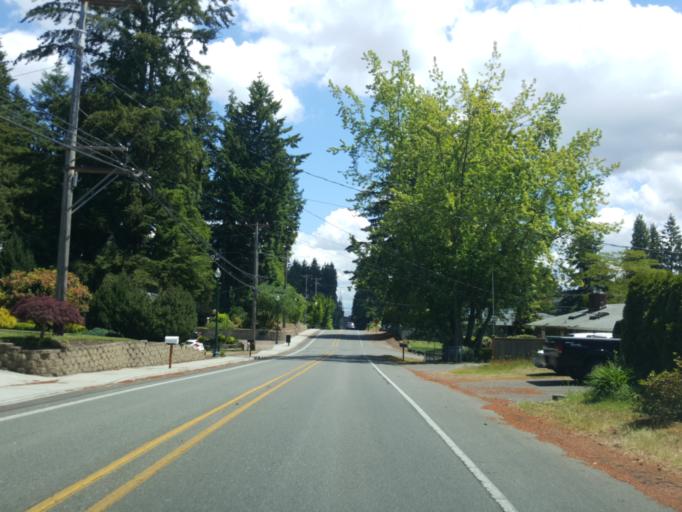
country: US
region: Washington
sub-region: Pierce County
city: University Place
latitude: 47.2172
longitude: -122.5315
